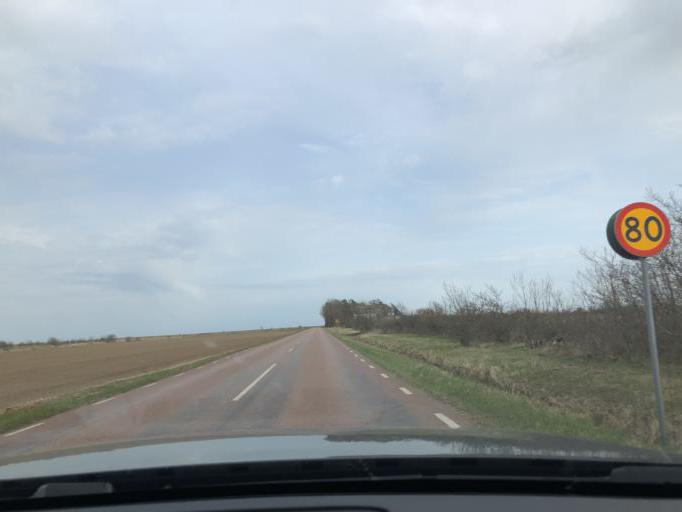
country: SE
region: Kalmar
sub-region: Morbylanga Kommun
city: Moerbylanga
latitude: 56.2881
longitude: 16.4835
